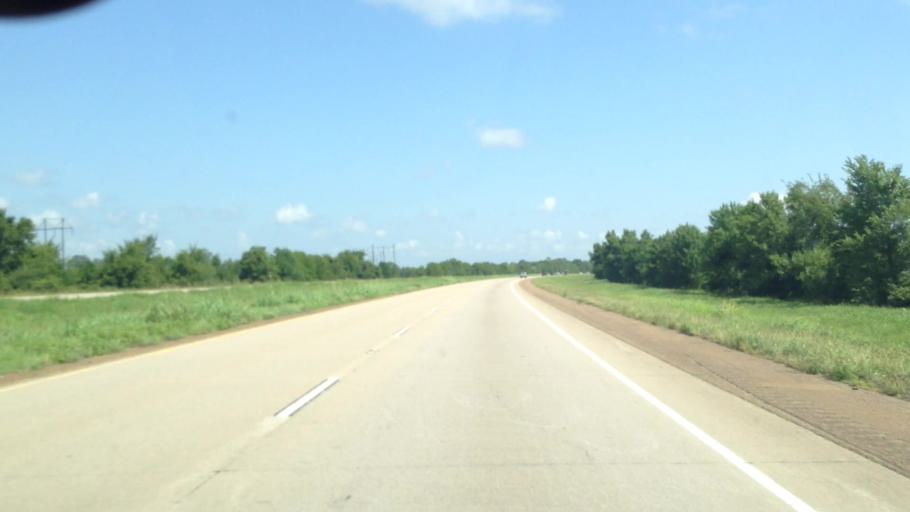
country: US
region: Louisiana
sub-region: Rapides Parish
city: Woodworth
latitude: 31.1867
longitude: -92.4718
